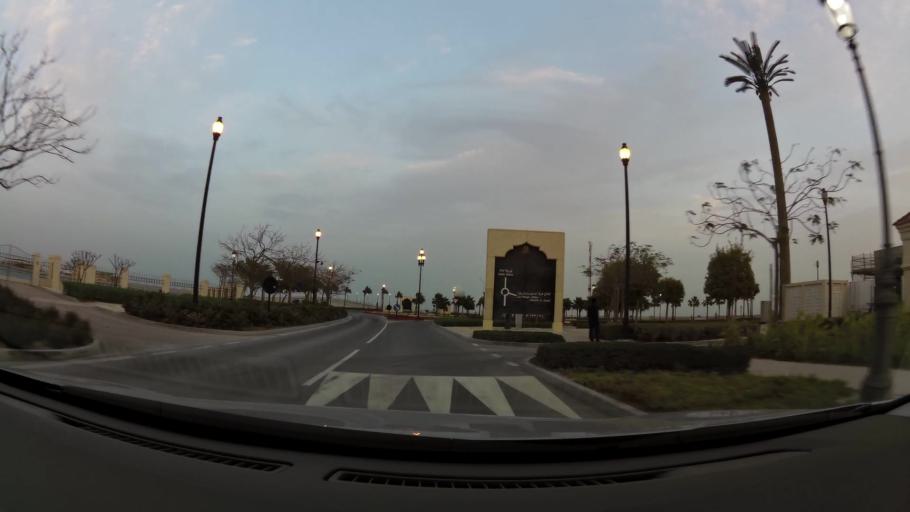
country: QA
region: Baladiyat ad Dawhah
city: Doha
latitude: 25.3594
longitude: 51.5688
